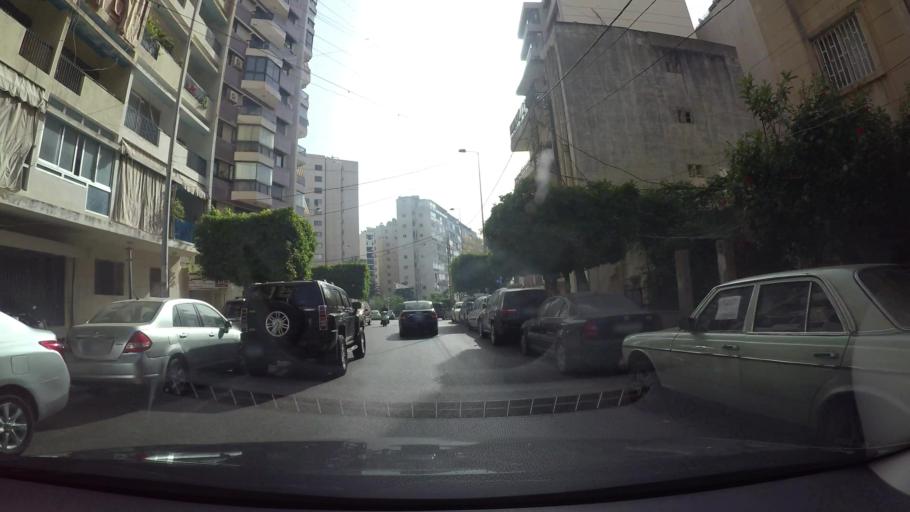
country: LB
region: Beyrouth
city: Ra's Bayrut
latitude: 33.8959
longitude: 35.4754
